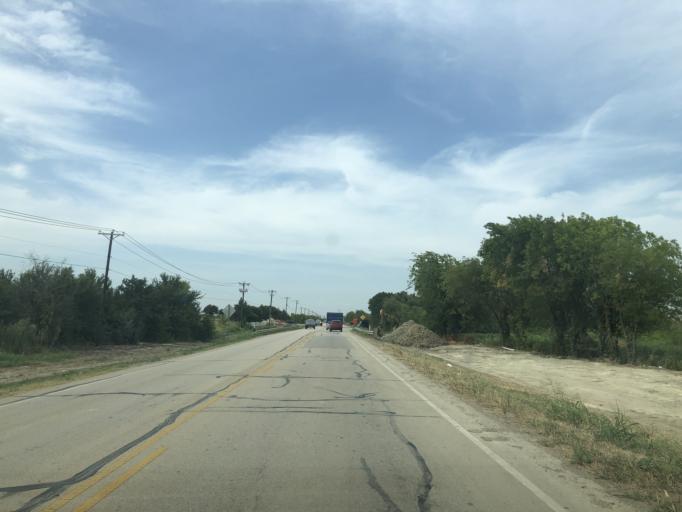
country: US
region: Texas
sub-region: Tarrant County
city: Saginaw
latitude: 32.9048
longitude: -97.3489
